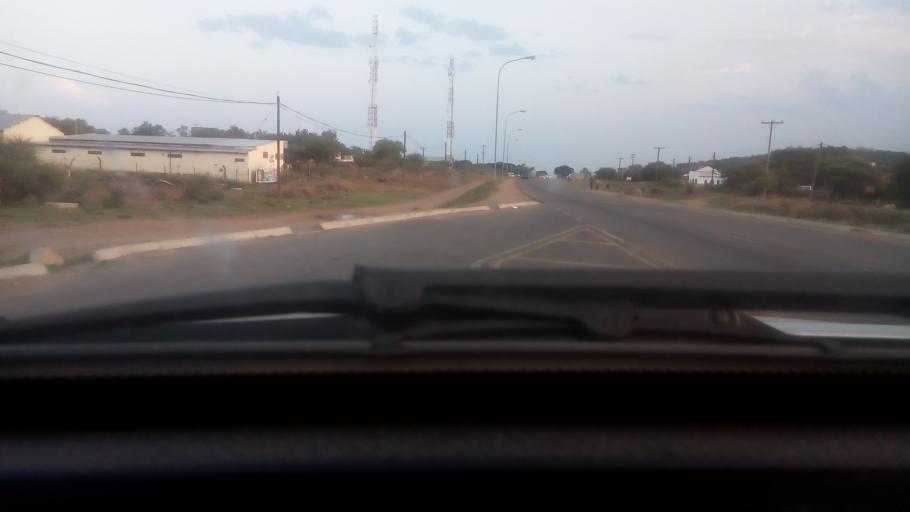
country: BW
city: Pilane
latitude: -24.4027
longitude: 26.0800
